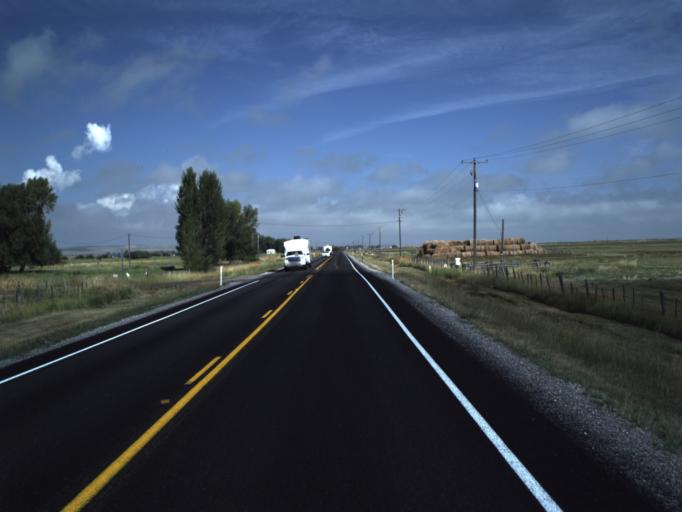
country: US
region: Utah
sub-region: Rich County
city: Randolph
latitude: 41.6279
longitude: -111.1791
